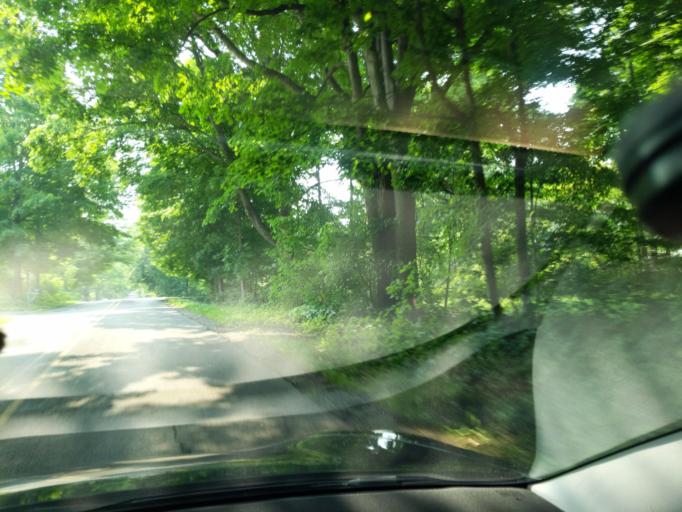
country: US
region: Michigan
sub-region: Ingham County
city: Holt
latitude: 42.6114
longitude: -84.5679
